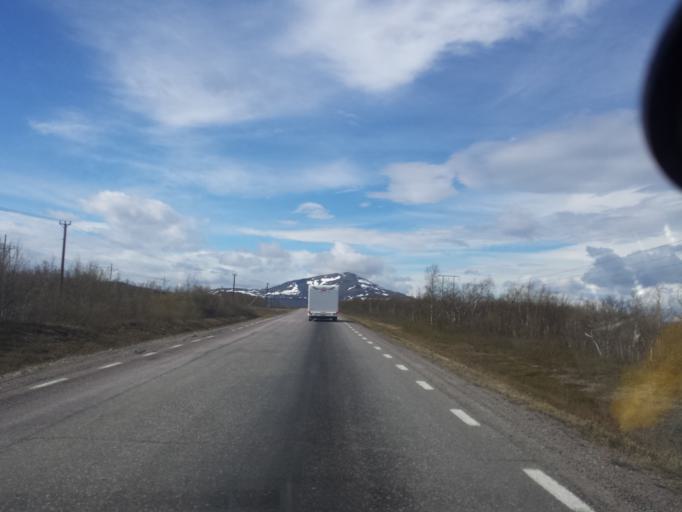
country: SE
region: Norrbotten
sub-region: Kiruna Kommun
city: Kiruna
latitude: 68.1142
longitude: 19.8304
